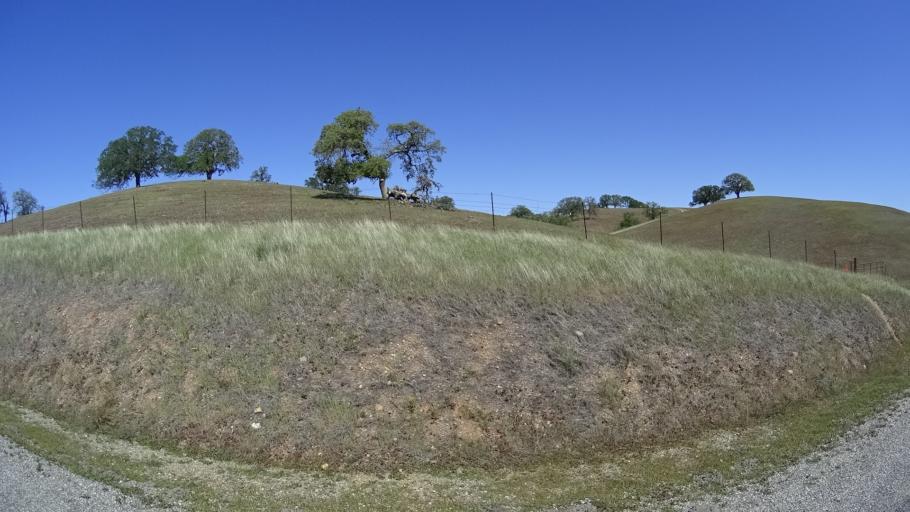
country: US
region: California
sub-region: Glenn County
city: Orland
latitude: 39.7423
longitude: -122.3814
